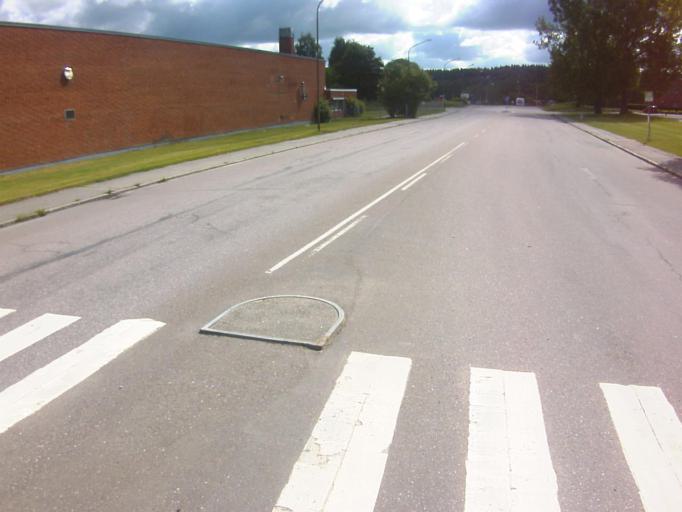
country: SE
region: Soedermanland
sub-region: Eskilstuna Kommun
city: Skogstorp
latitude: 59.3422
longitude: 16.4824
